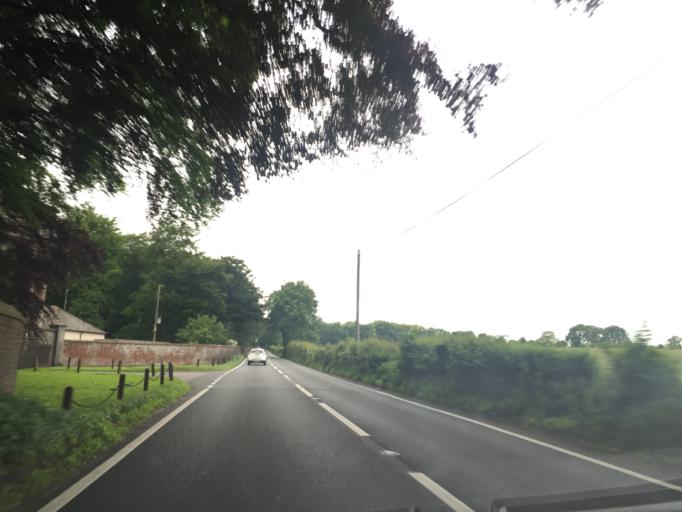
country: GB
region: England
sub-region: Dorset
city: Lytchett Matravers
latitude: 50.7893
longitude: -2.0910
